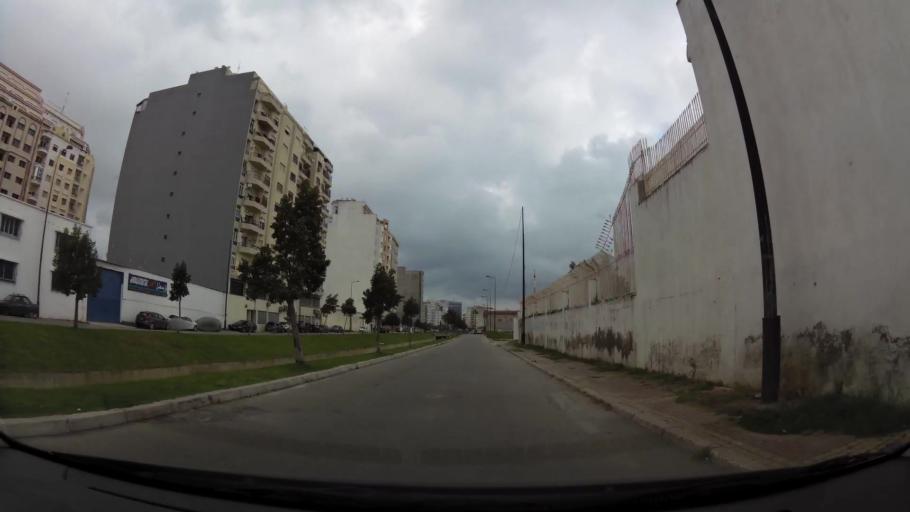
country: MA
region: Tanger-Tetouan
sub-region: Tanger-Assilah
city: Tangier
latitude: 35.7672
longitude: -5.8039
